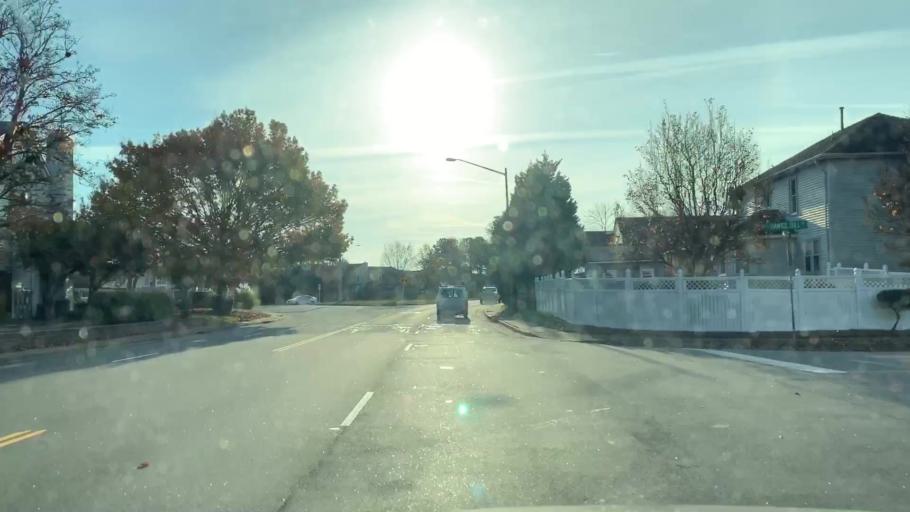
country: US
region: Virginia
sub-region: City of Chesapeake
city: Chesapeake
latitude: 36.7900
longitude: -76.1651
